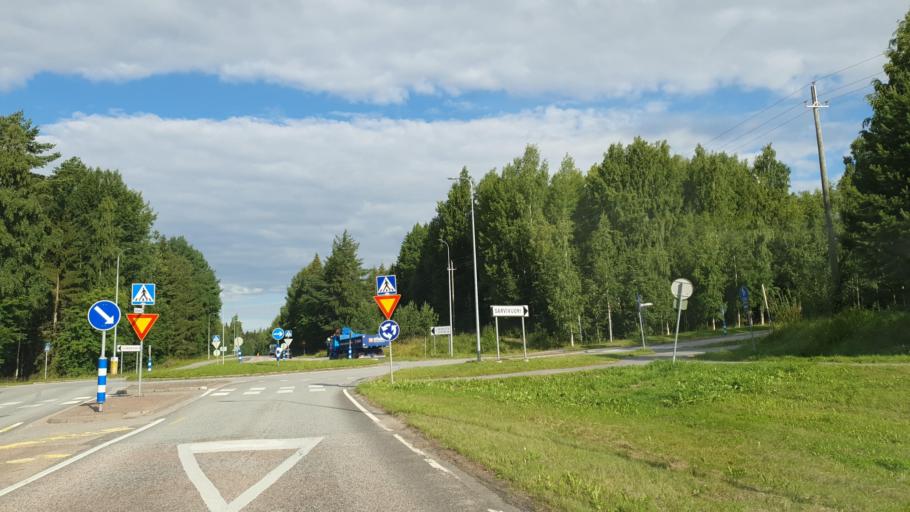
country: FI
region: Central Finland
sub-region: Jyvaeskylae
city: Saeynaetsalo
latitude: 62.1795
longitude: 25.7319
